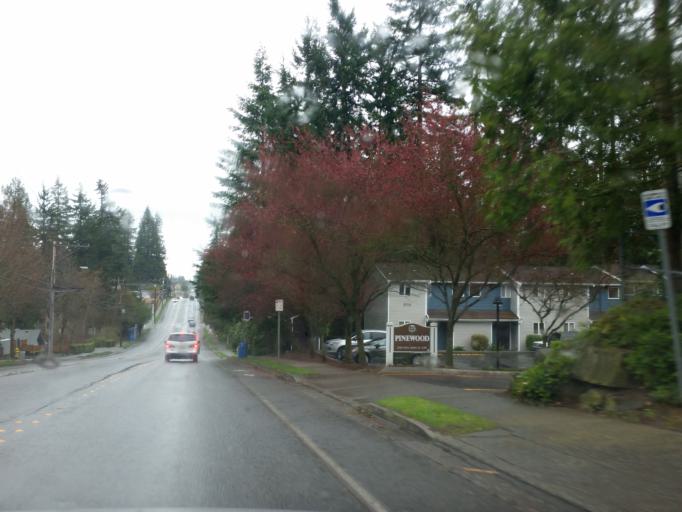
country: US
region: Washington
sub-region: Snohomish County
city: Lynnwood
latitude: 47.8175
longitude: -122.3115
